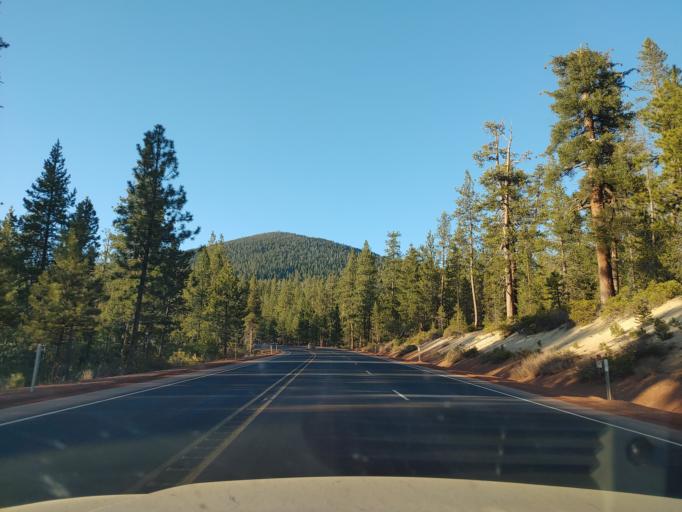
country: US
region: Oregon
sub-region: Deschutes County
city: La Pine
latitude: 43.4471
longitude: -121.8697
